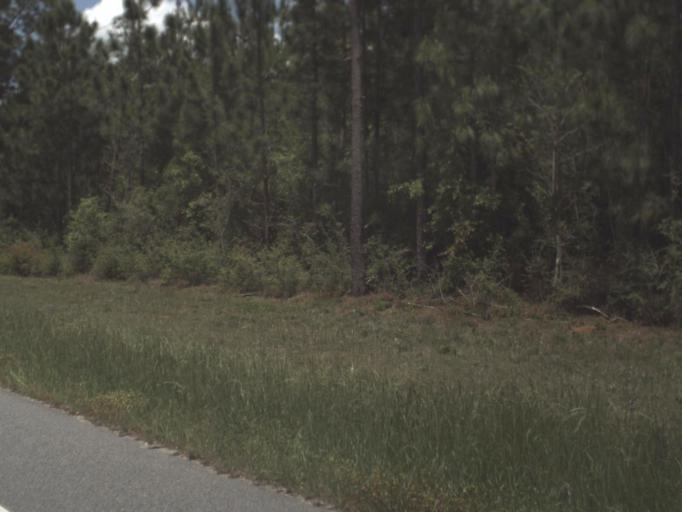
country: US
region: Florida
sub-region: Escambia County
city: Molino
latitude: 30.7597
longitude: -87.3811
